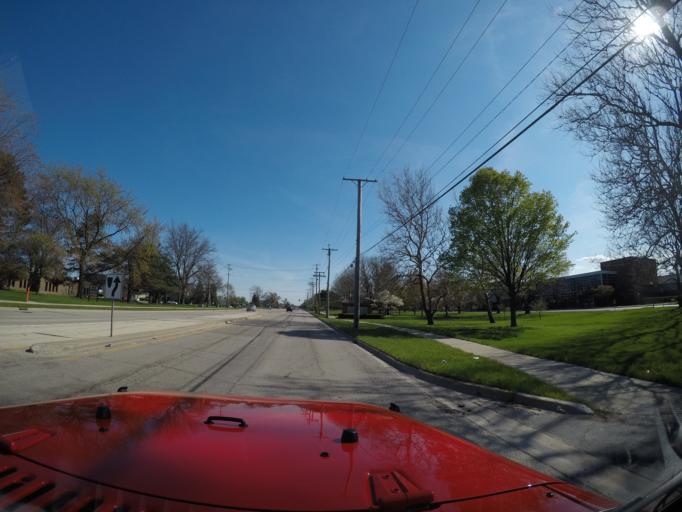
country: US
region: Illinois
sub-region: Cook County
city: Northbrook
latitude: 42.1117
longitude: -87.8295
